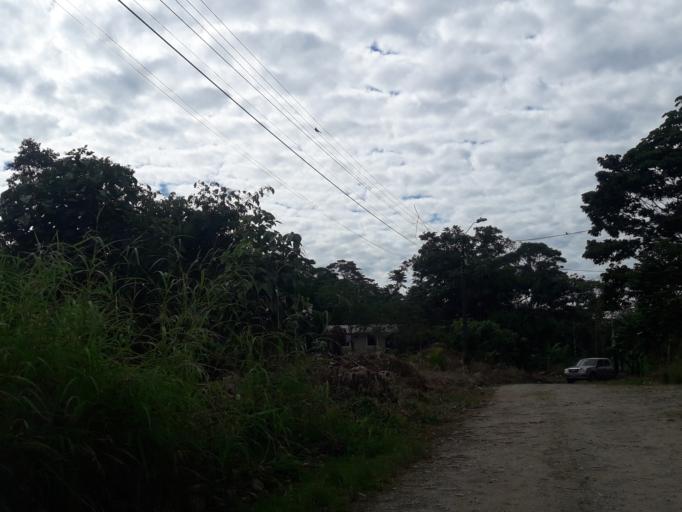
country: EC
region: Napo
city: Tena
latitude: -0.9820
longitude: -77.8218
